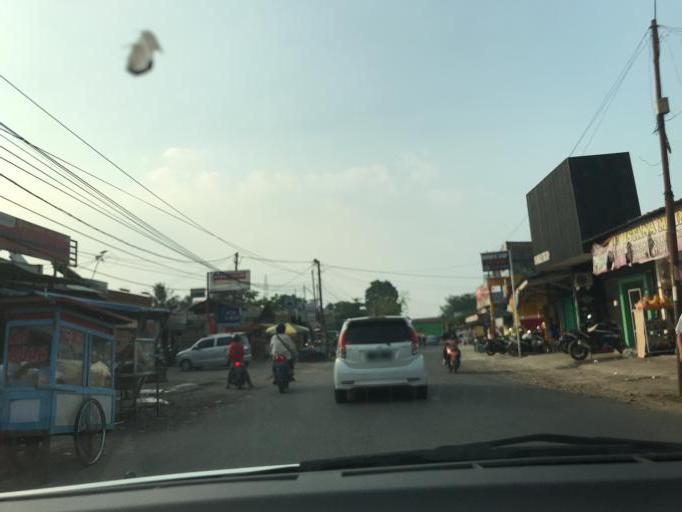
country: ID
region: West Java
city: Cibinong
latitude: -6.4782
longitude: 106.8182
